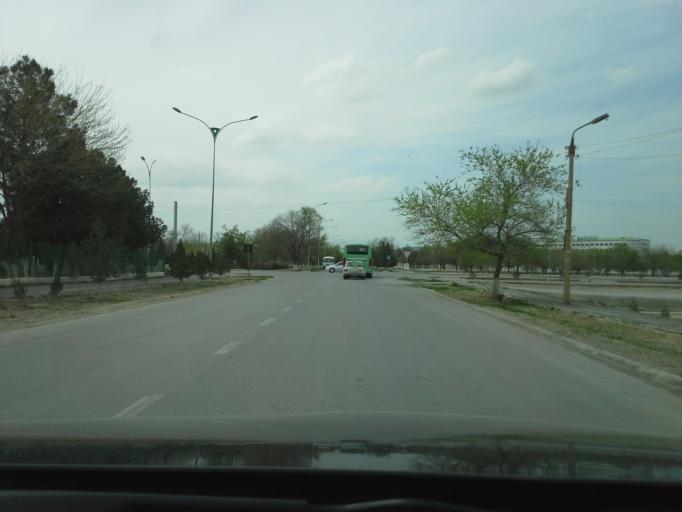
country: TM
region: Ahal
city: Abadan
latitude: 38.0587
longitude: 58.1474
